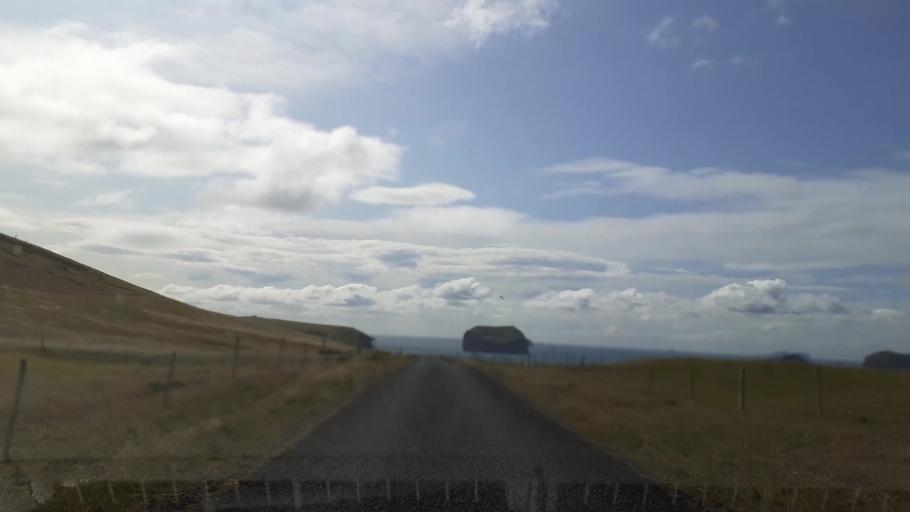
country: IS
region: South
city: Vestmannaeyjar
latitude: 63.4217
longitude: -20.2787
